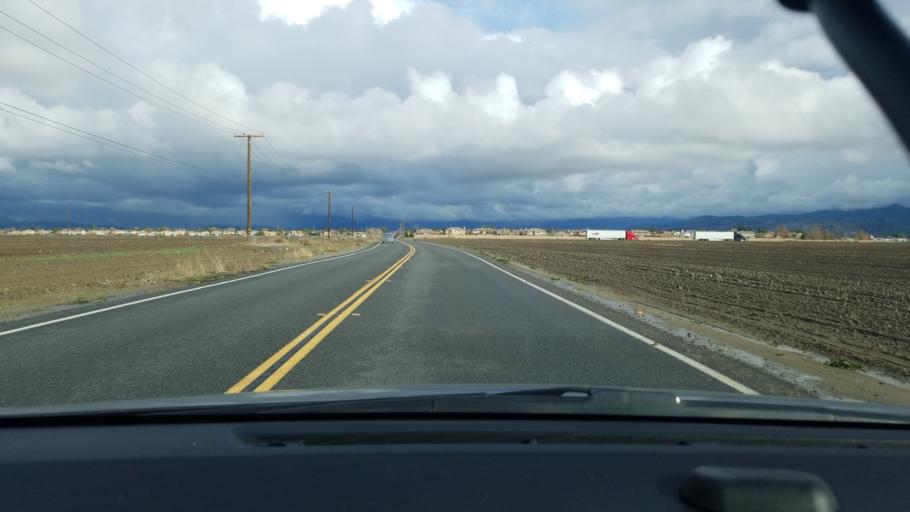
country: US
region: California
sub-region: Riverside County
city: Green Acres
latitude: 33.7509
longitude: -117.0273
